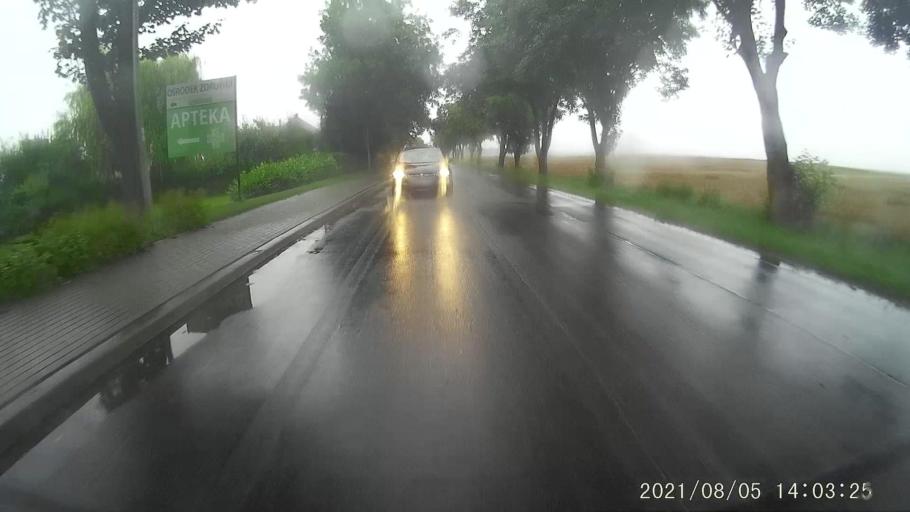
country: PL
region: Opole Voivodeship
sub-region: Powiat krapkowicki
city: Strzeleczki
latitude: 50.4580
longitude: 17.8577
